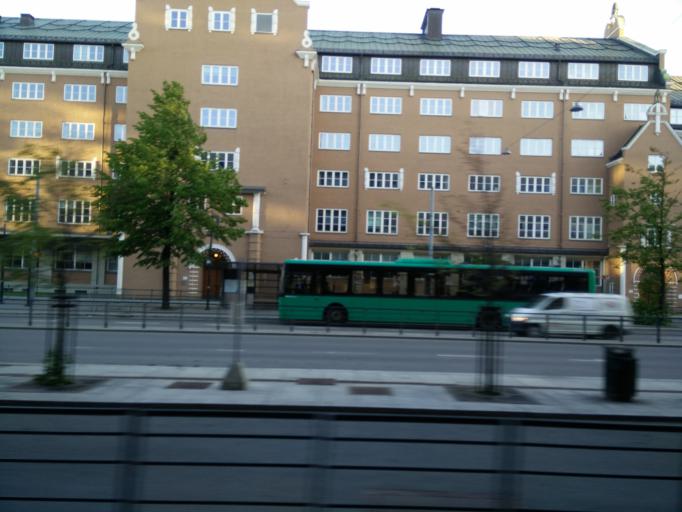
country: NO
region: Oslo
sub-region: Oslo
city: Oslo
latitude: 59.9112
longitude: 10.7596
